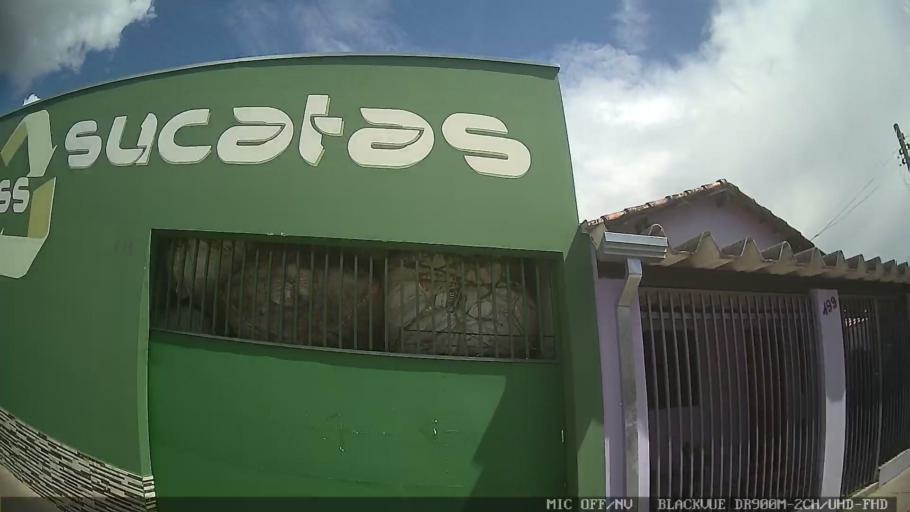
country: BR
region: Sao Paulo
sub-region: Conchas
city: Conchas
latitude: -23.0249
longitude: -48.0123
